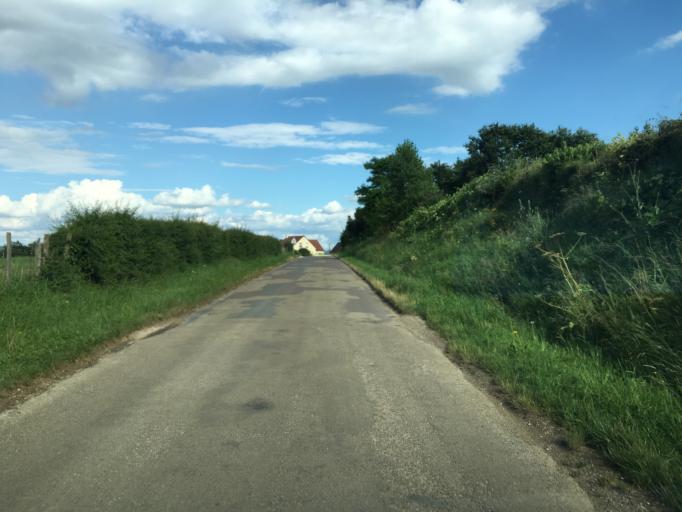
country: FR
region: Bourgogne
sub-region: Departement de l'Yonne
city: Appoigny
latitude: 47.8821
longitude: 3.5172
